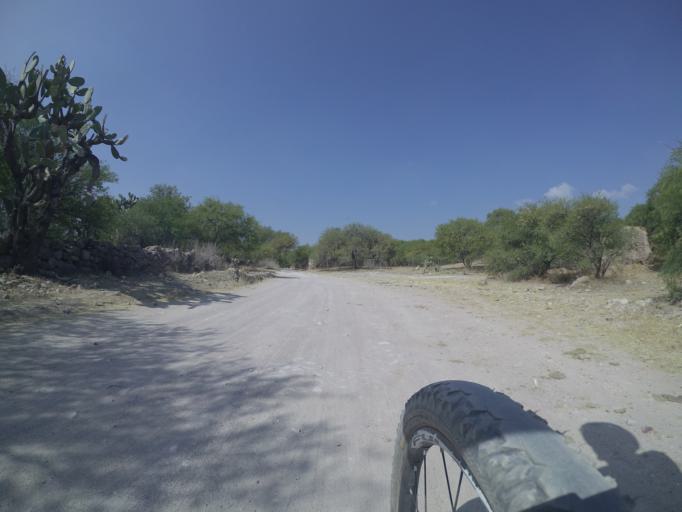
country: MX
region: Aguascalientes
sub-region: Jesus Maria
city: Paseos de las Haciendas [Fraccionamiento]
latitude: 21.9986
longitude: -102.3583
